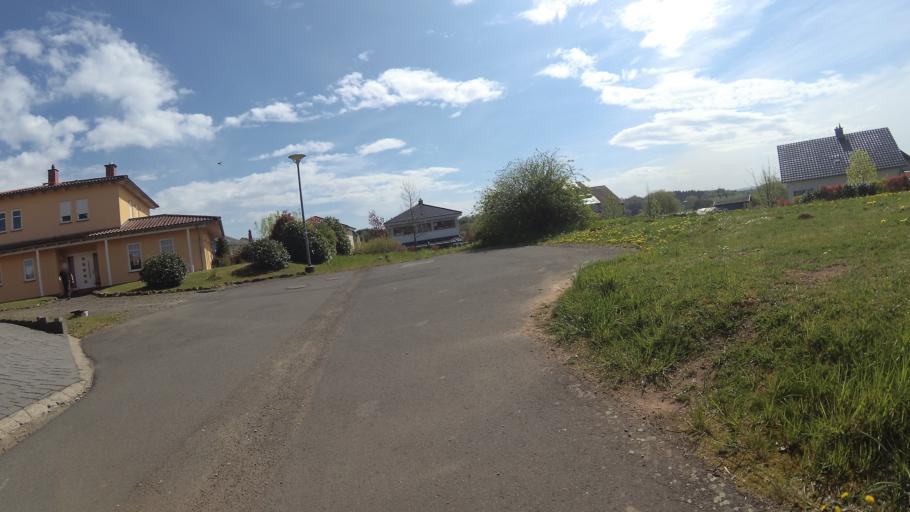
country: DE
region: Saarland
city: Oberthal
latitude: 49.4785
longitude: 7.1080
